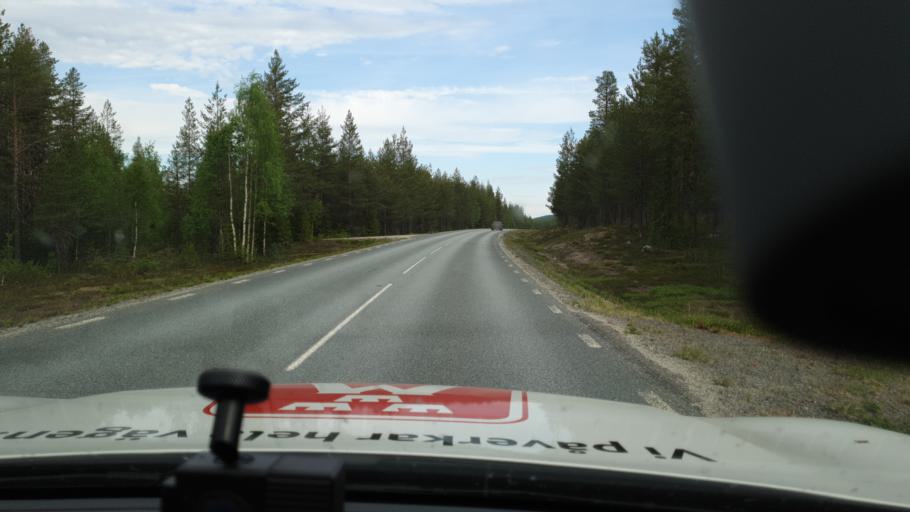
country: SE
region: Vaesterbotten
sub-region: Mala Kommun
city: Mala
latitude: 65.0028
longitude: 18.4684
